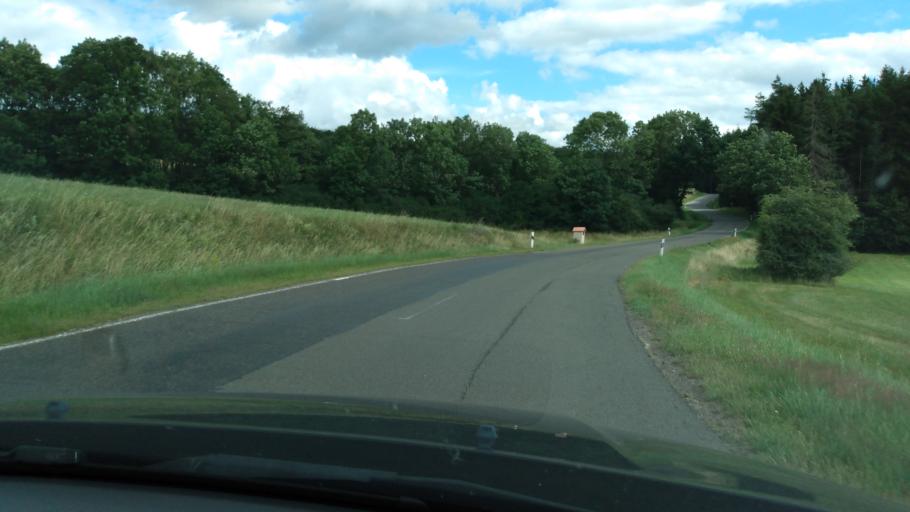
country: DE
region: Rheinland-Pfalz
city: Karl
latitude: 50.0566
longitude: 6.7910
